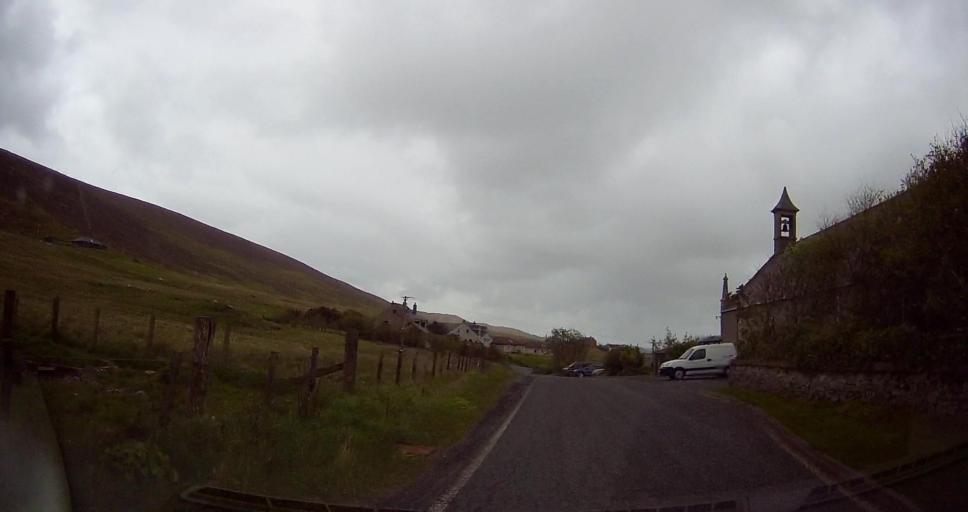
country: GB
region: Scotland
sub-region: Shetland Islands
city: Lerwick
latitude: 60.2561
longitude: -1.2893
